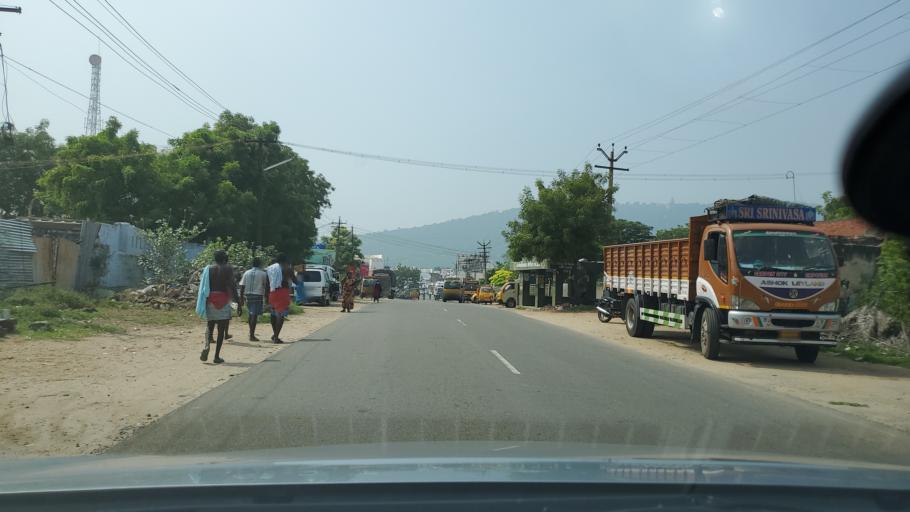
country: IN
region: Tamil Nadu
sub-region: Erode
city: Chennimalai
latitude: 11.1695
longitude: 77.6034
